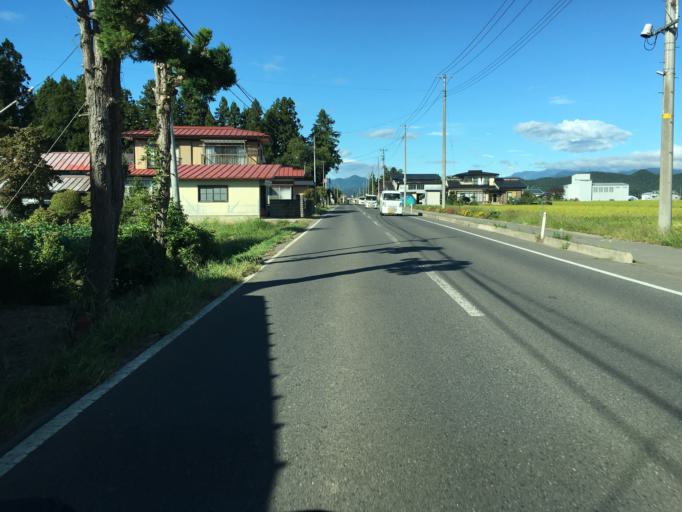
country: JP
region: Yamagata
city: Takahata
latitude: 37.9673
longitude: 140.1580
